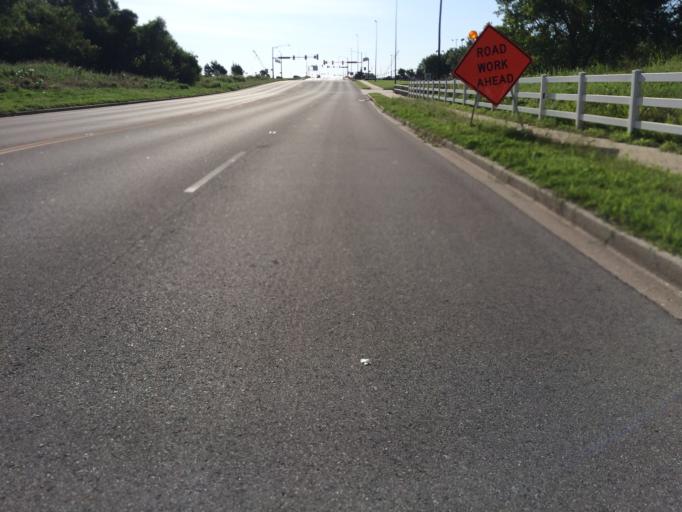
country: US
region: Oklahoma
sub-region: Cleveland County
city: Norman
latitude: 35.2039
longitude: -97.4861
